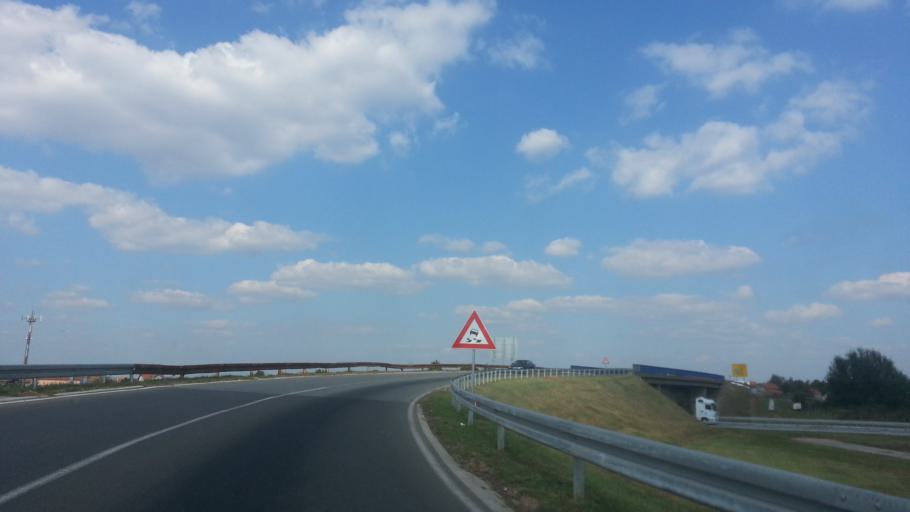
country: RS
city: Novi Banovci
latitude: 44.9424
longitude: 20.2811
